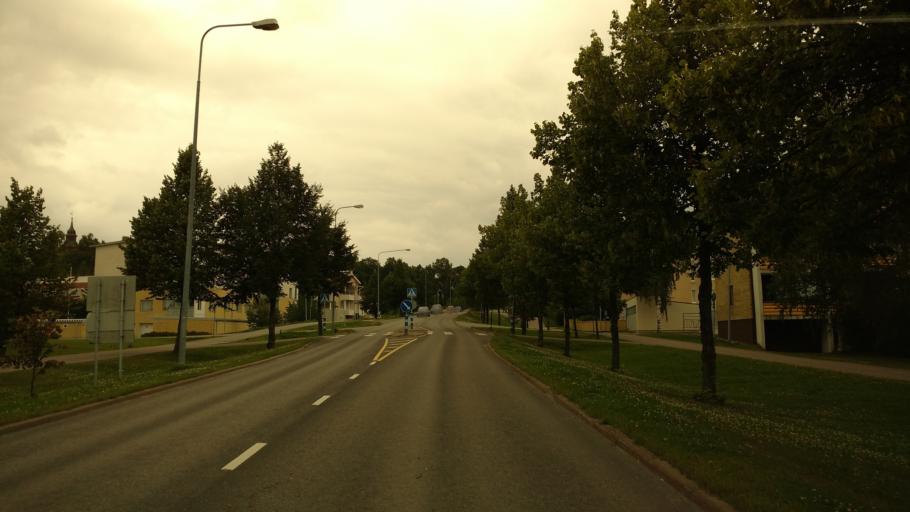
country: FI
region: Varsinais-Suomi
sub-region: Salo
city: Halikko
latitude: 60.3980
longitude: 23.0768
